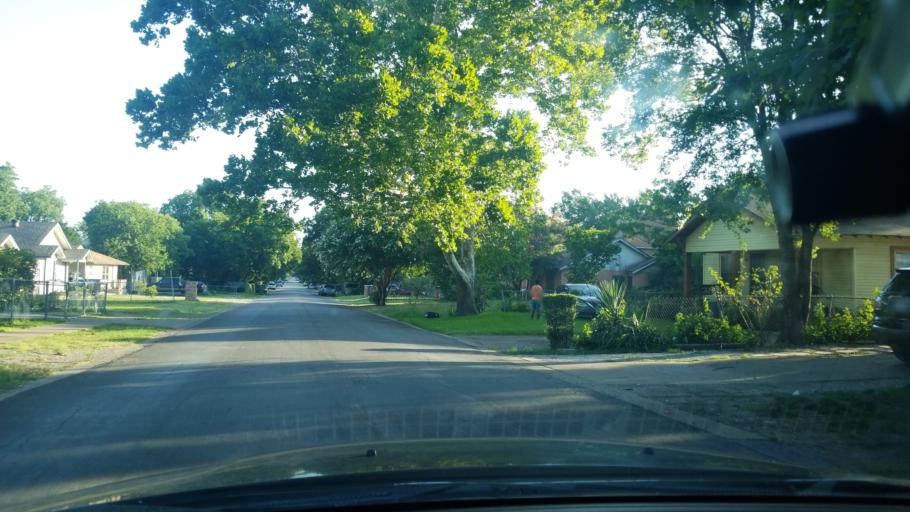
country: US
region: Texas
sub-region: Dallas County
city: Cockrell Hill
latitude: 32.7151
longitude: -96.8218
